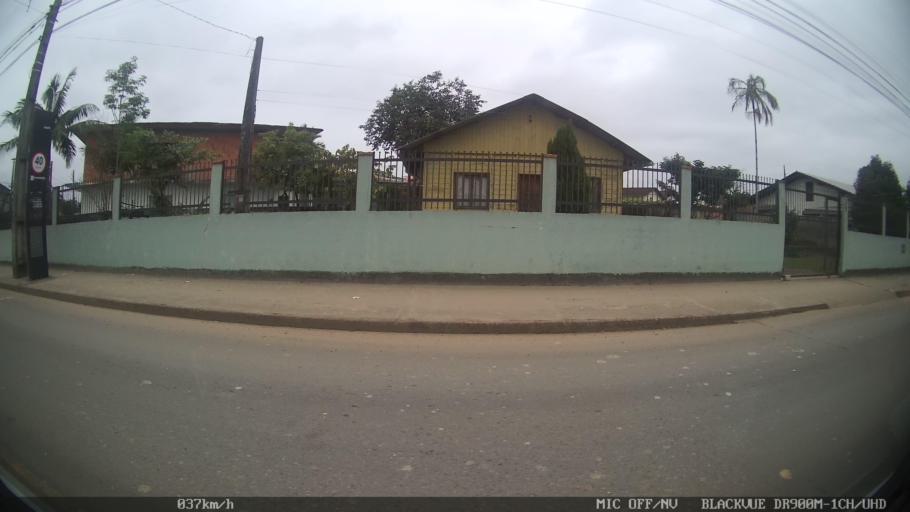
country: BR
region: Santa Catarina
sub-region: Joinville
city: Joinville
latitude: -26.3384
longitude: -48.8228
